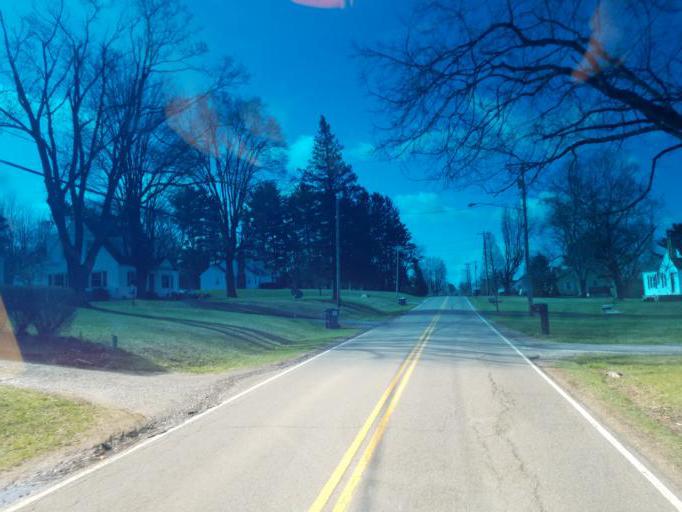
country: US
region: Ohio
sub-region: Knox County
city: Mount Vernon
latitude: 40.4138
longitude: -82.4951
